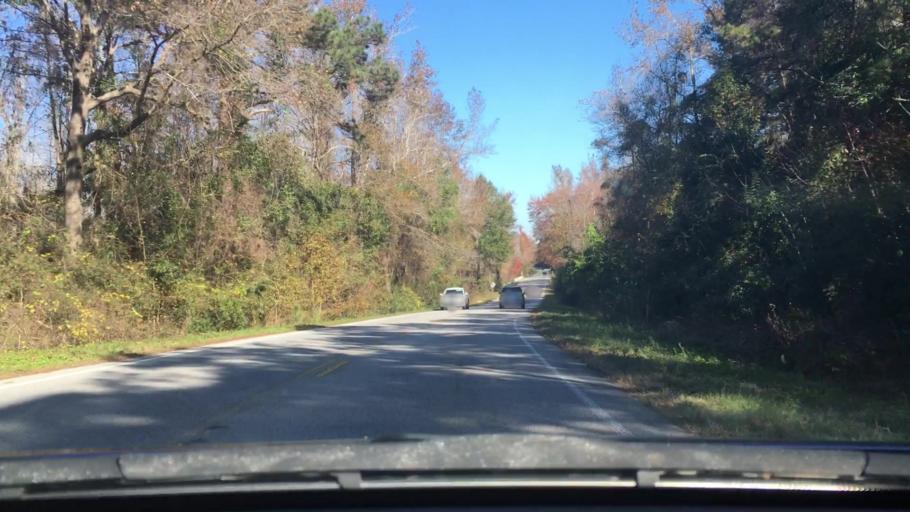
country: US
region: South Carolina
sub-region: Sumter County
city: Lakewood
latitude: 33.8766
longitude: -80.3672
